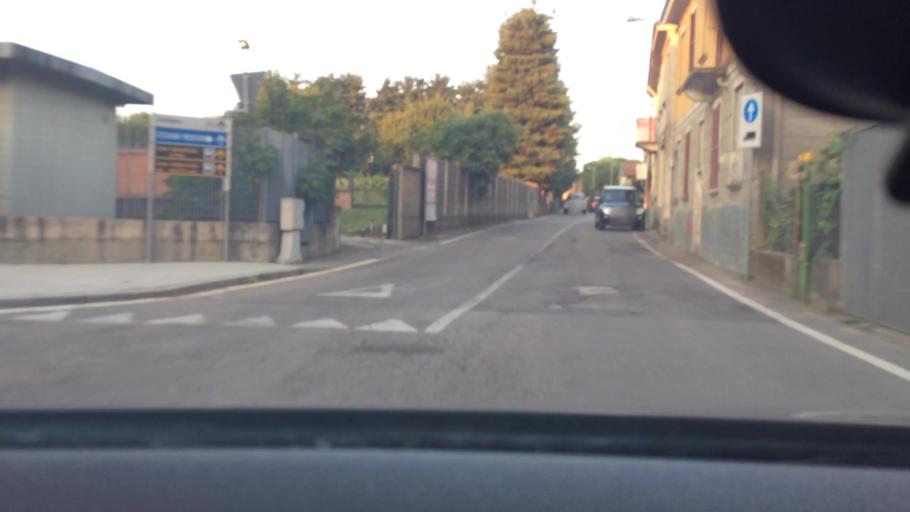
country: IT
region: Lombardy
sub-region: Provincia di Monza e Brianza
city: Ceriano Laghetto
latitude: 45.6263
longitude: 9.0809
